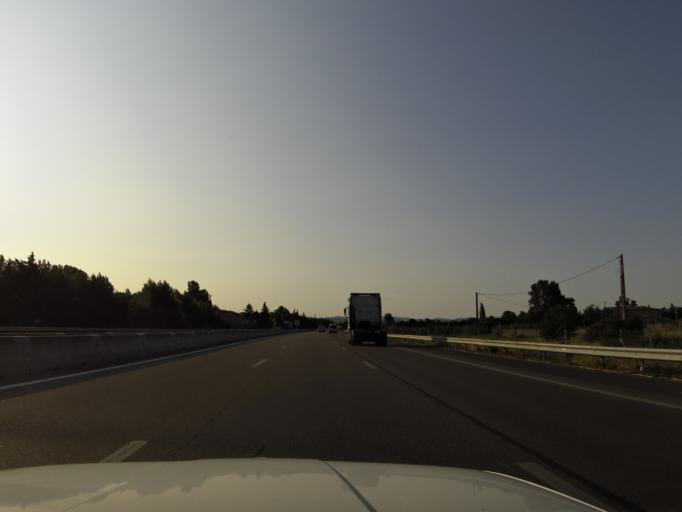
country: FR
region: Rhone-Alpes
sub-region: Departement de la Drome
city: Saulce-sur-Rhone
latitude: 44.6900
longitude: 4.7919
